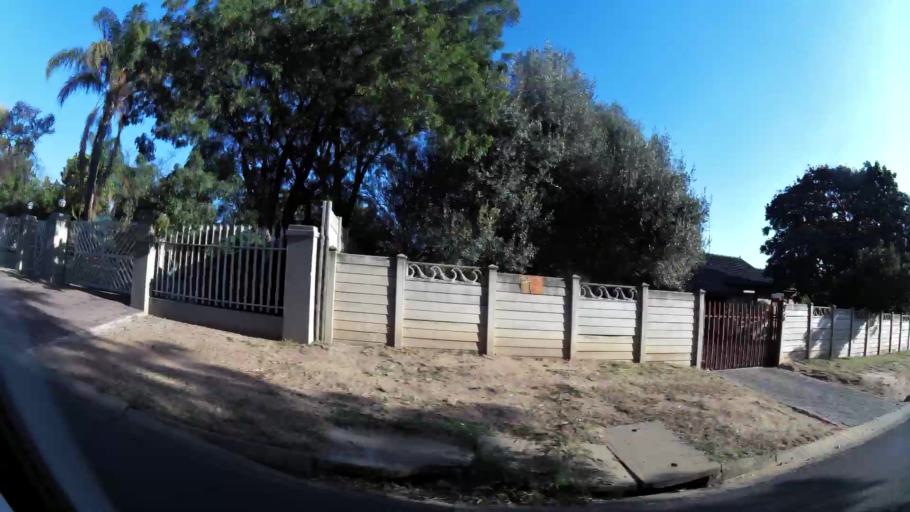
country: ZA
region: North-West
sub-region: Bojanala Platinum District Municipality
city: Rustenburg
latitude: -25.6869
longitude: 27.2372
